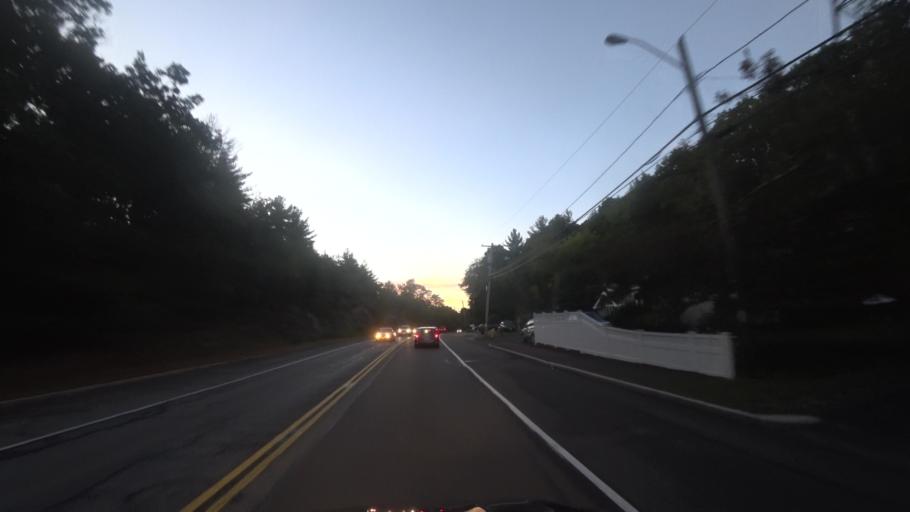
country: US
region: Massachusetts
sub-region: Middlesex County
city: Melrose
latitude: 42.4846
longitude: -71.0437
